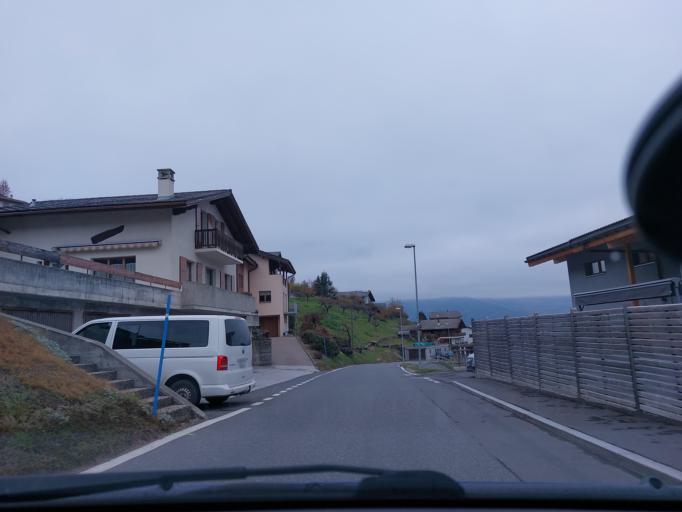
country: CH
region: Valais
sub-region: Conthey District
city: Basse-Nendaz
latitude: 46.1920
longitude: 7.3095
